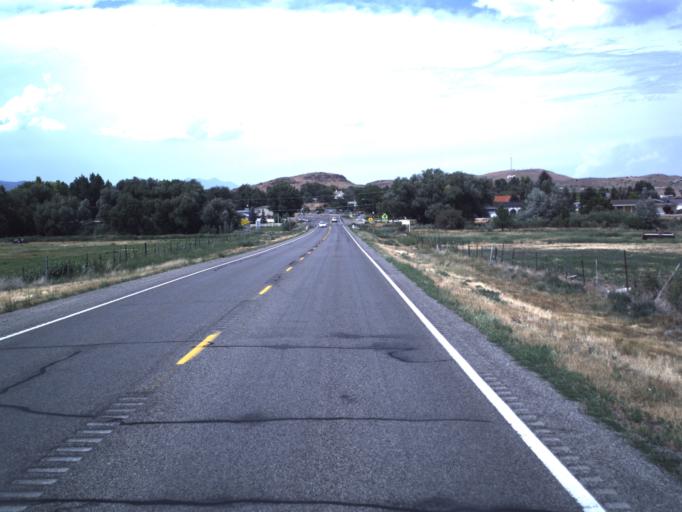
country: US
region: Utah
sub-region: Sanpete County
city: Moroni
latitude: 39.5210
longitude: -111.5746
